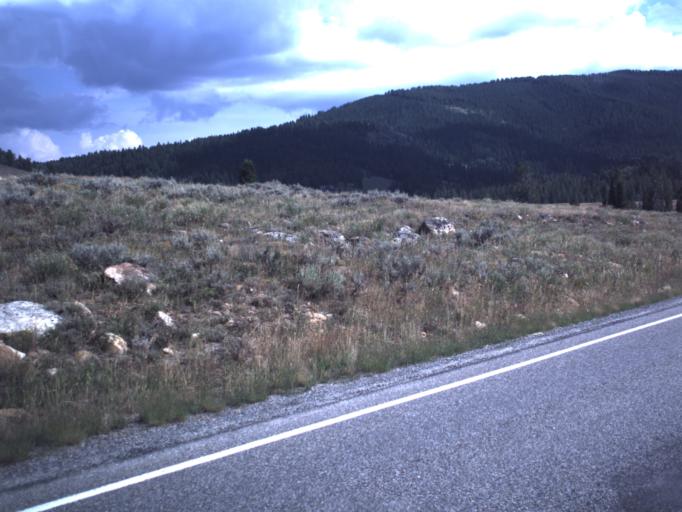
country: US
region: Utah
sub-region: Cache County
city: Richmond
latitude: 41.9675
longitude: -111.5319
